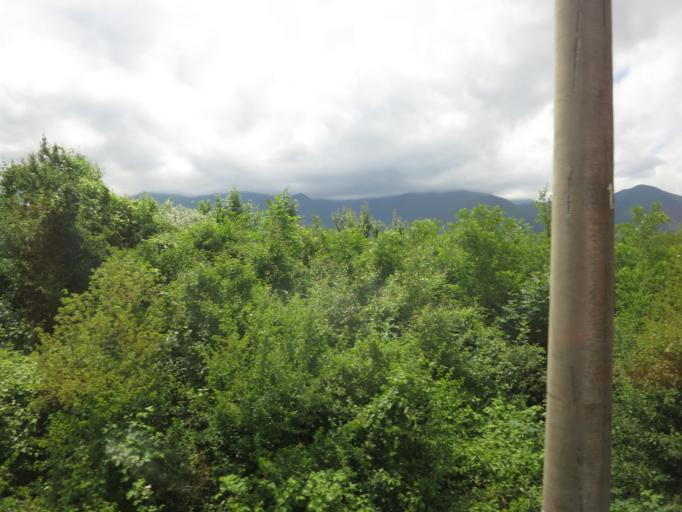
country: GE
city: Surami
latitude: 41.9915
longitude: 43.5648
